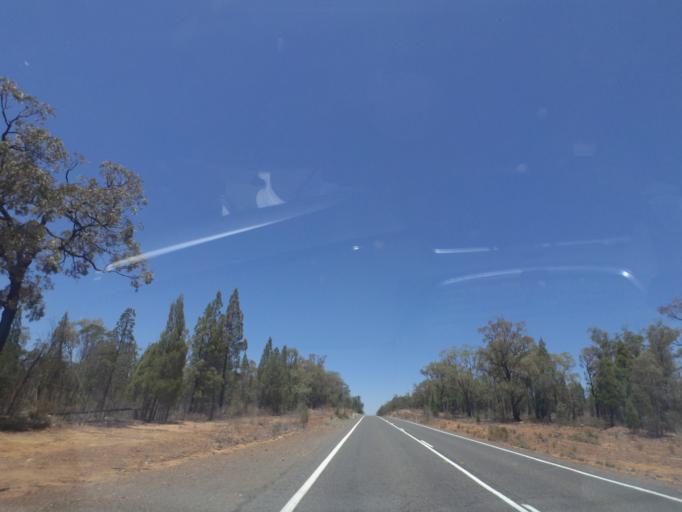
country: AU
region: New South Wales
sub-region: Narrabri
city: Narrabri
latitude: -30.7018
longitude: 149.5342
